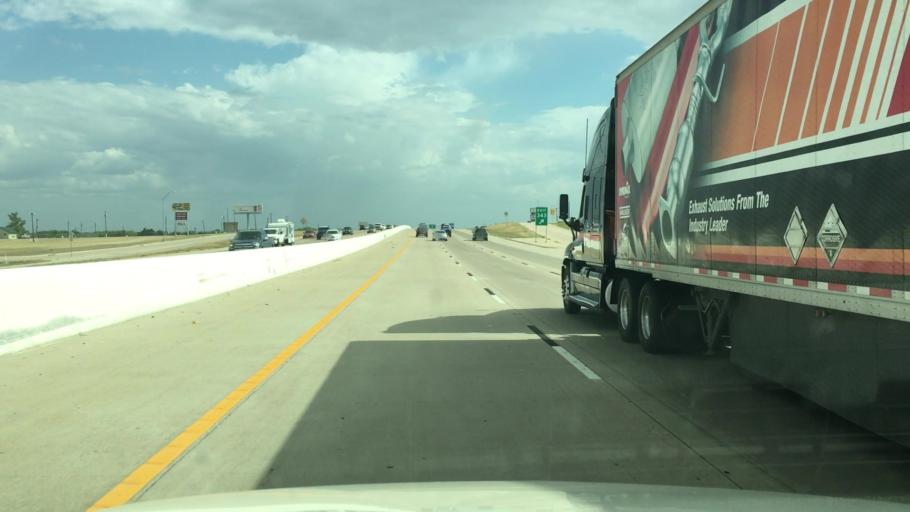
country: US
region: Texas
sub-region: McLennan County
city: Northcrest
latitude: 31.6840
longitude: -97.0999
